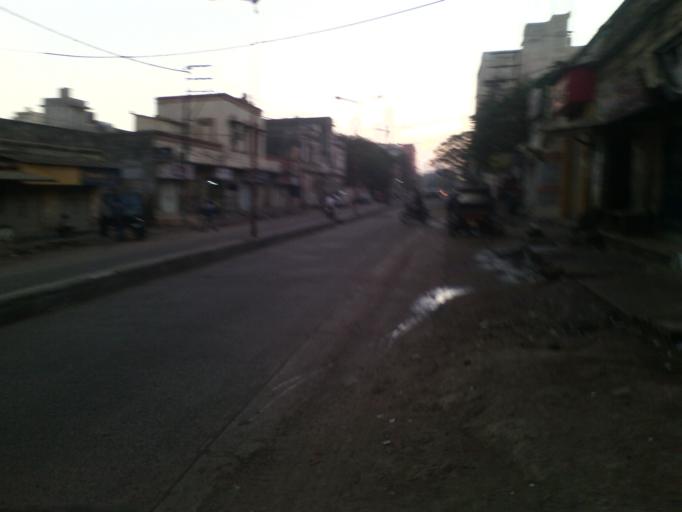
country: IN
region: Gujarat
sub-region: Porbandar
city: Porbandar
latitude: 21.6402
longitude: 69.6079
